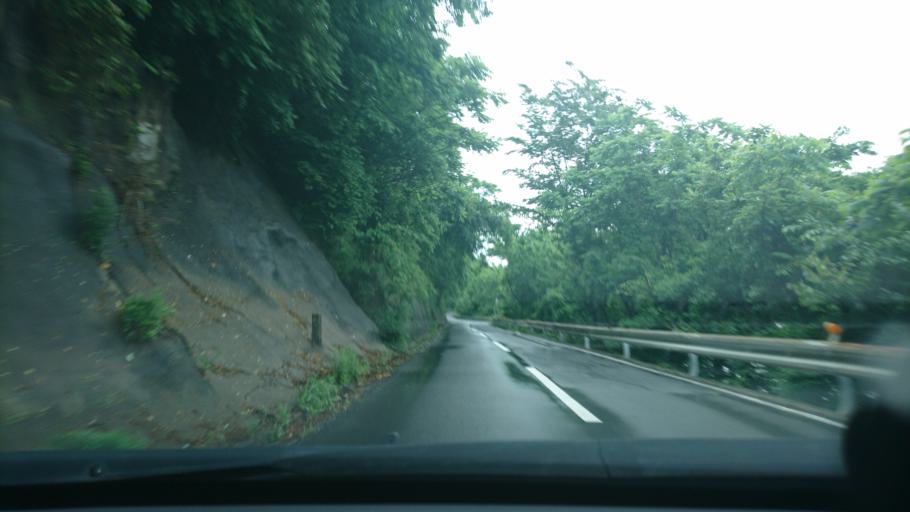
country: JP
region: Miyagi
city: Wakuya
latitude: 38.6812
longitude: 141.2846
